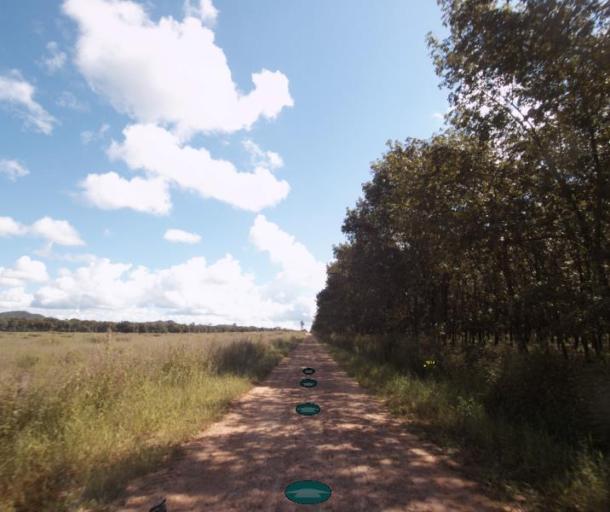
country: BR
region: Goias
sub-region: Pirenopolis
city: Pirenopolis
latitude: -15.7787
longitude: -49.0398
